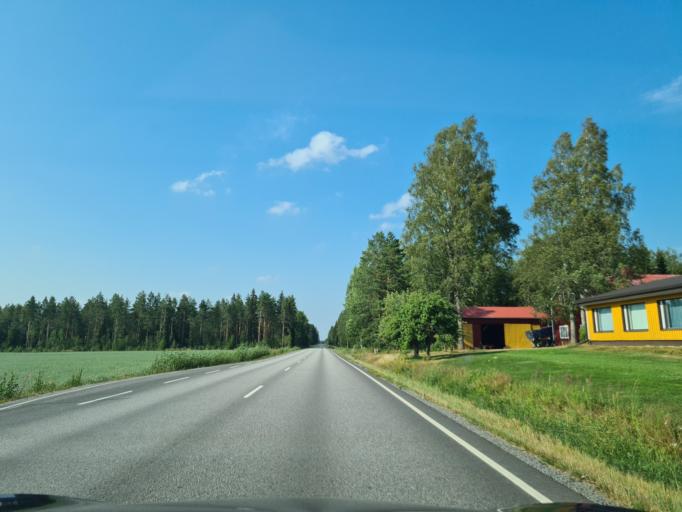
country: FI
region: Satakunta
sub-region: Pohjois-Satakunta
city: Karvia
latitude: 62.0372
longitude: 22.5144
